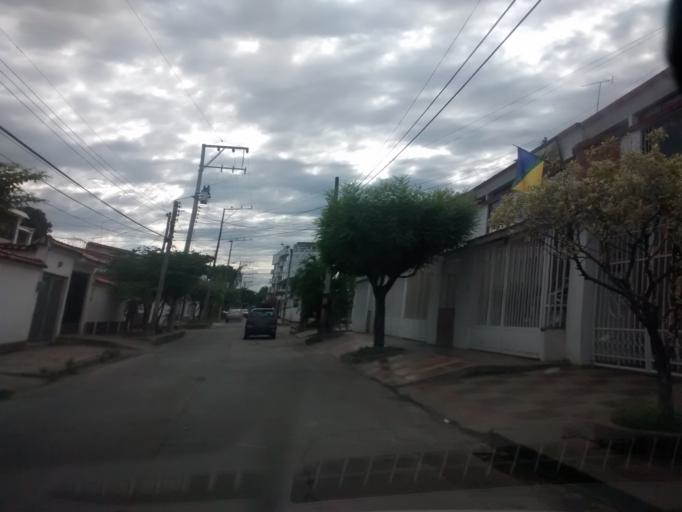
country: CO
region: Cundinamarca
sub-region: Girardot
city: Girardot City
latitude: 4.3076
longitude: -74.7994
